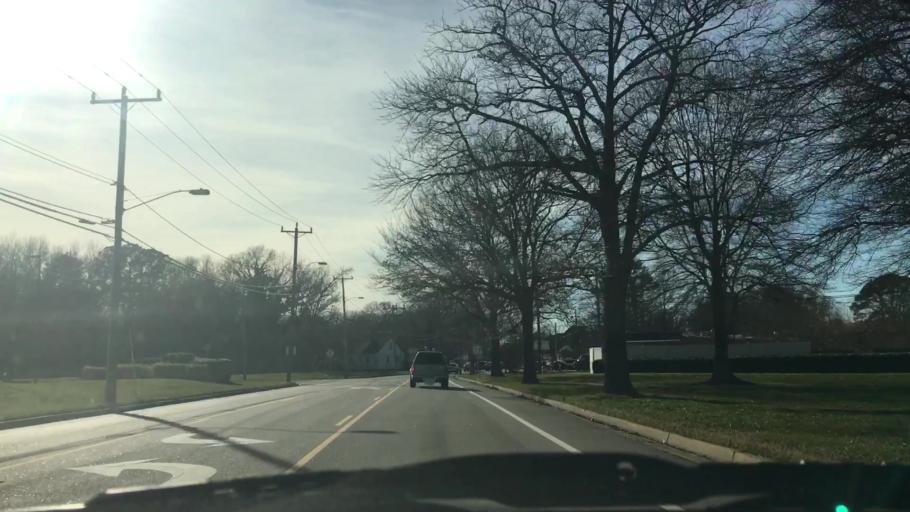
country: US
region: Virginia
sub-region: City of Norfolk
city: Norfolk
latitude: 36.8794
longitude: -76.2248
